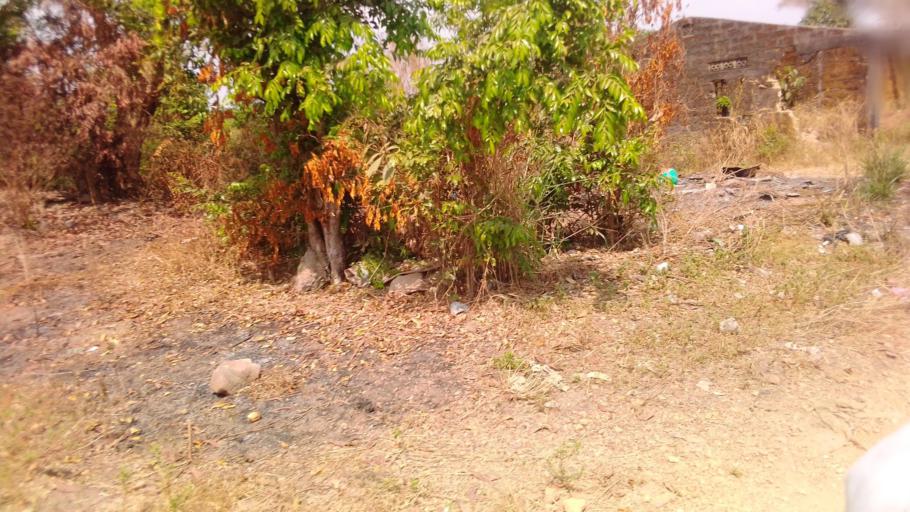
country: SL
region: Southern Province
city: Mogbwemo
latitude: 7.7978
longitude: -12.2962
